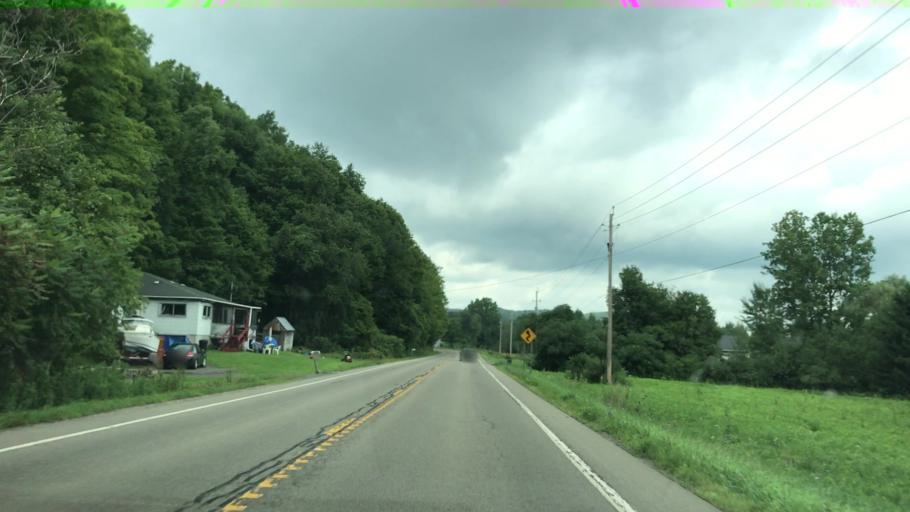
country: US
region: New York
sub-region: Steuben County
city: Bath
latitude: 42.3989
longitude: -77.3488
